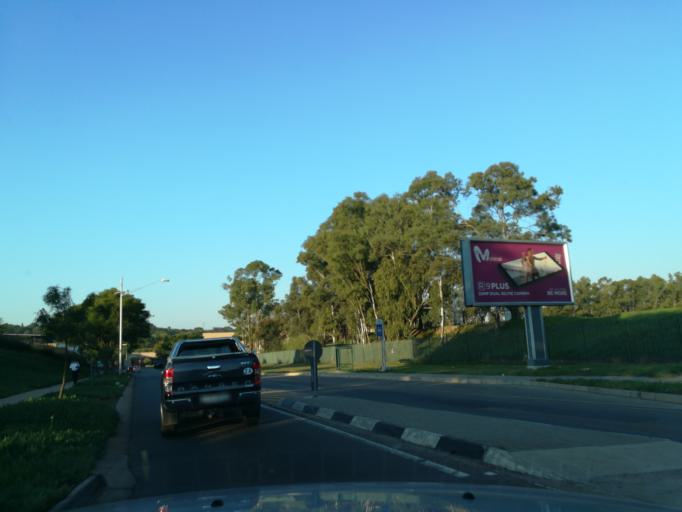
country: ZA
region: Gauteng
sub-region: City of Tshwane Metropolitan Municipality
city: Pretoria
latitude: -25.7679
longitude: 28.2198
